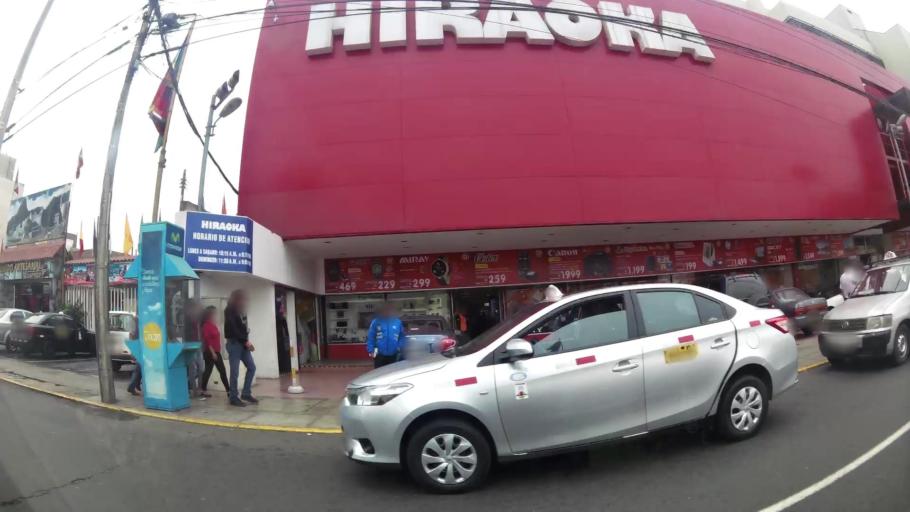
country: PE
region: Lima
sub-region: Lima
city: San Isidro
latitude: -12.1153
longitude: -77.0283
